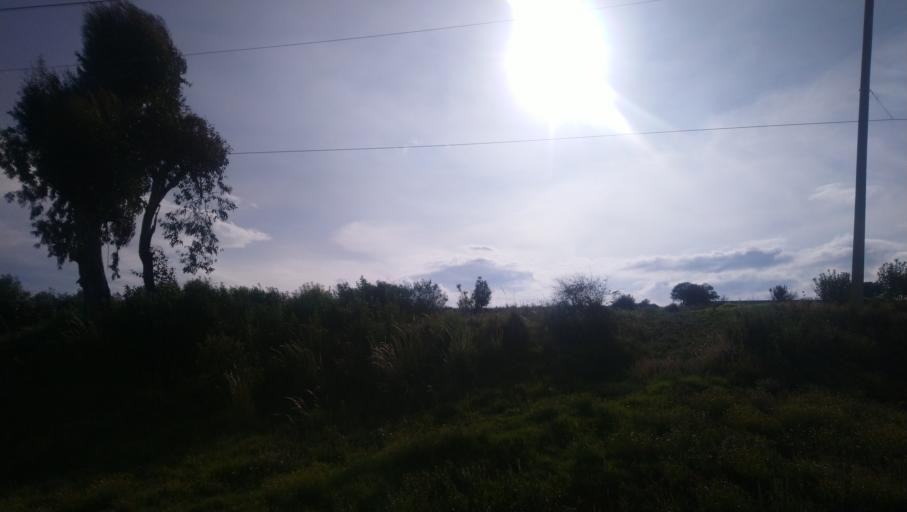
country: MX
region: Mexico
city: Juchitepec de Mariano Riva Palacio
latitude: 19.1211
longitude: -98.9373
